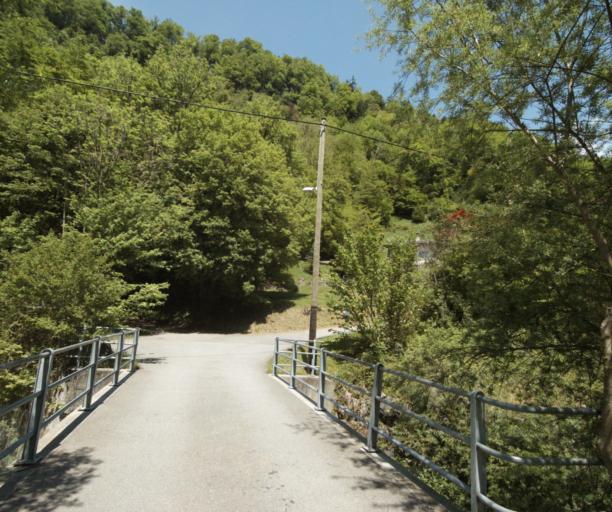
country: CH
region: Vaud
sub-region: Aigle District
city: Villeneuve
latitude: 46.4042
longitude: 6.9416
